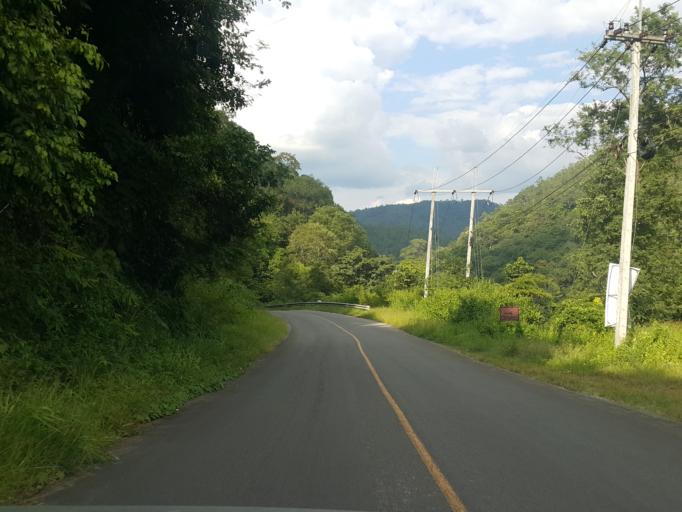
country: TH
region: Chiang Mai
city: Mae Chaem
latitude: 18.5421
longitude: 98.3793
